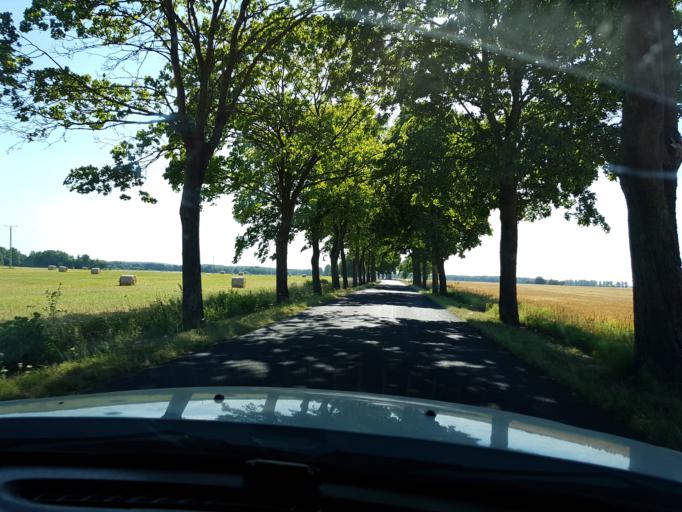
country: PL
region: West Pomeranian Voivodeship
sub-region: Powiat bialogardzki
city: Bialogard
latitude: 53.9858
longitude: 15.9348
